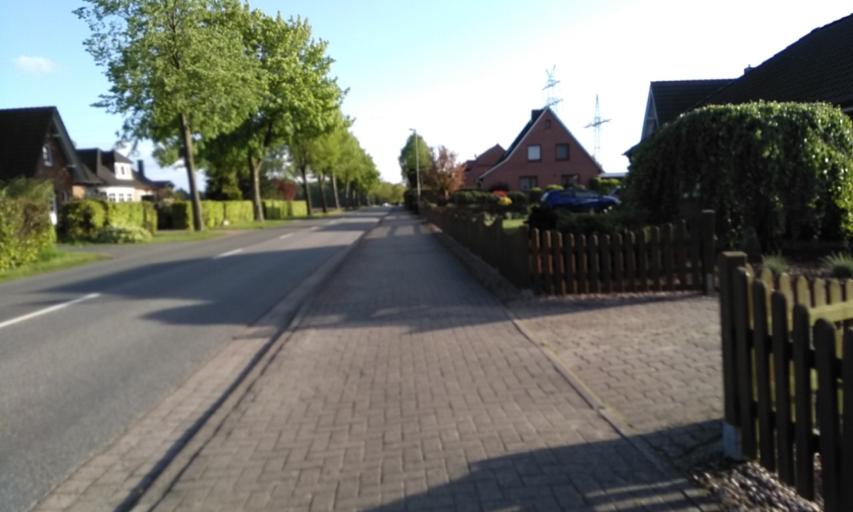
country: DE
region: Lower Saxony
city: Wohnste
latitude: 53.4060
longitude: 9.5441
